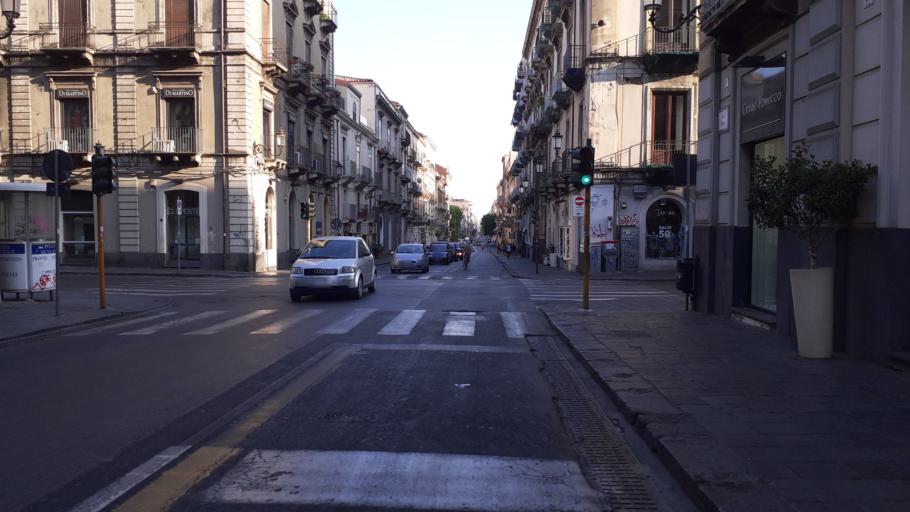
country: IT
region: Sicily
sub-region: Catania
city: Catania
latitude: 37.5135
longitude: 15.0847
